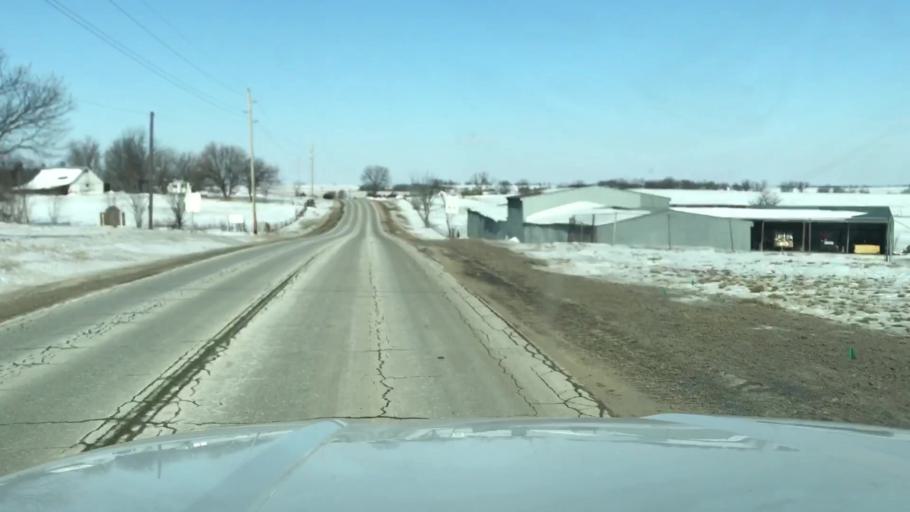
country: US
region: Missouri
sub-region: Andrew County
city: Savannah
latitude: 39.9547
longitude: -94.8486
